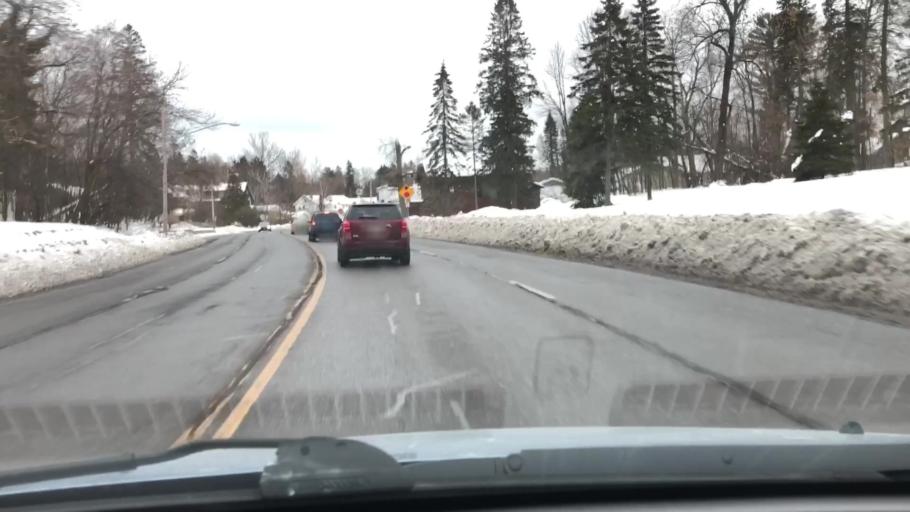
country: US
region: Minnesota
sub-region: Saint Louis County
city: Arnold
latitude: 46.8342
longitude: -92.0738
